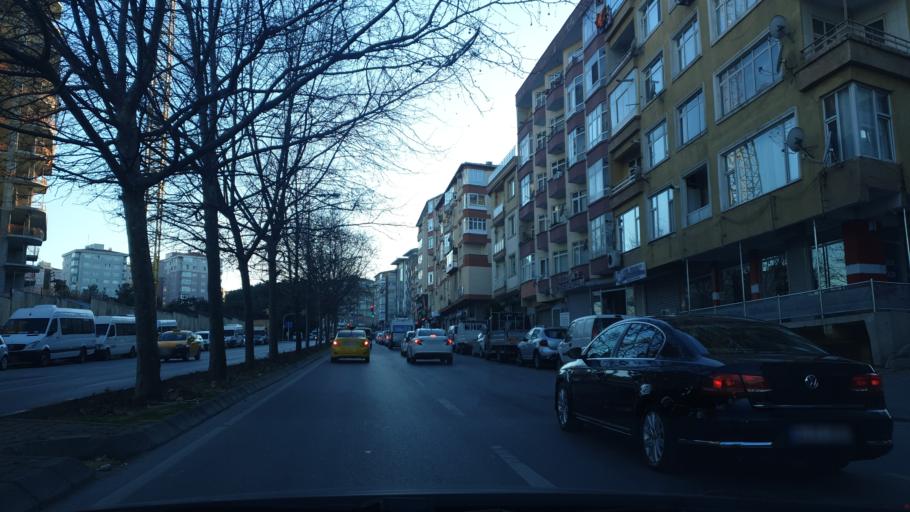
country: TR
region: Istanbul
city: merter keresteciler
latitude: 41.0116
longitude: 28.8771
